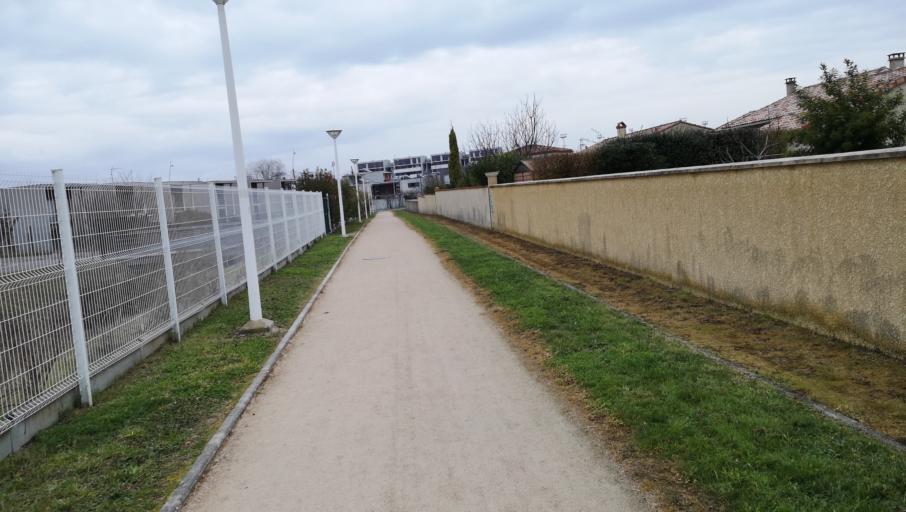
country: FR
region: Midi-Pyrenees
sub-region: Departement de la Haute-Garonne
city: Beauzelle
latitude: 43.6511
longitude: 1.3763
